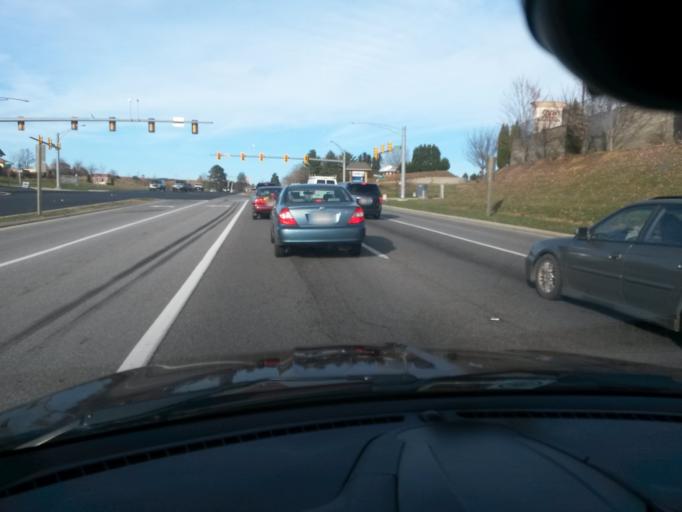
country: US
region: Virginia
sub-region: Botetourt County
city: Daleville
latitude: 37.4162
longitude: -79.9121
